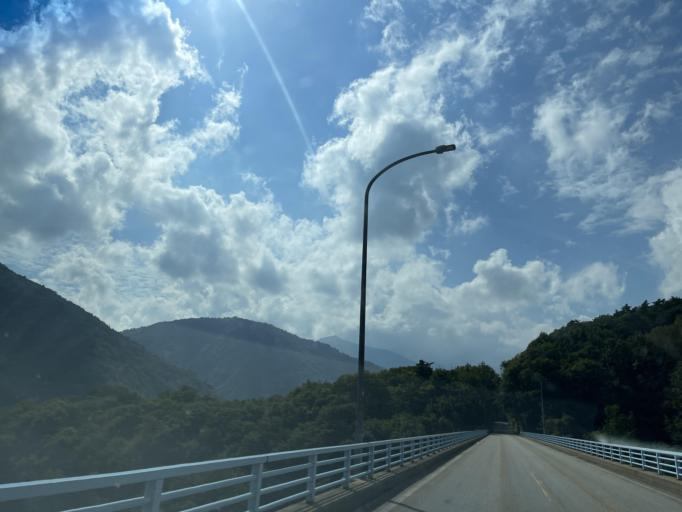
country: JP
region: Nagano
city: Omachi
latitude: 36.5194
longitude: 137.7823
